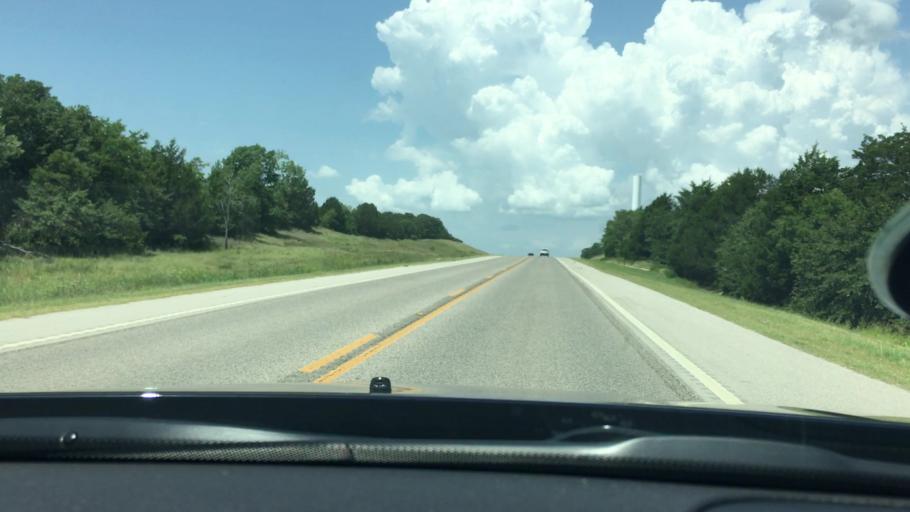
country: US
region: Oklahoma
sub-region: Carter County
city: Dickson
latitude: 34.1003
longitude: -96.9495
